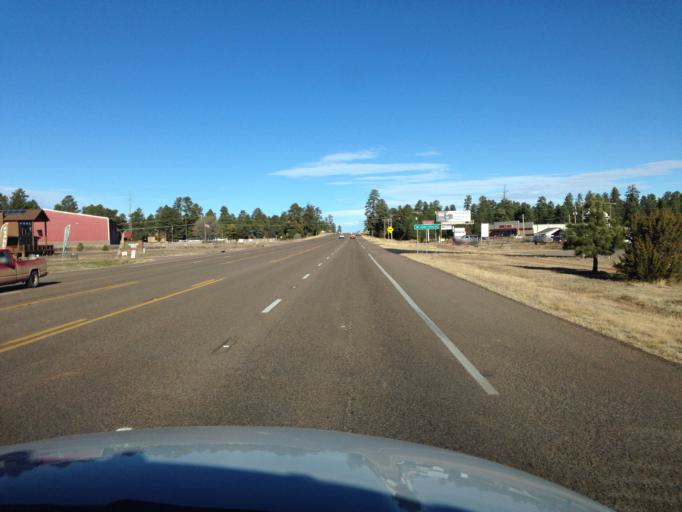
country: US
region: Arizona
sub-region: Navajo County
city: Heber-Overgaard
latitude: 34.4046
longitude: -110.5651
